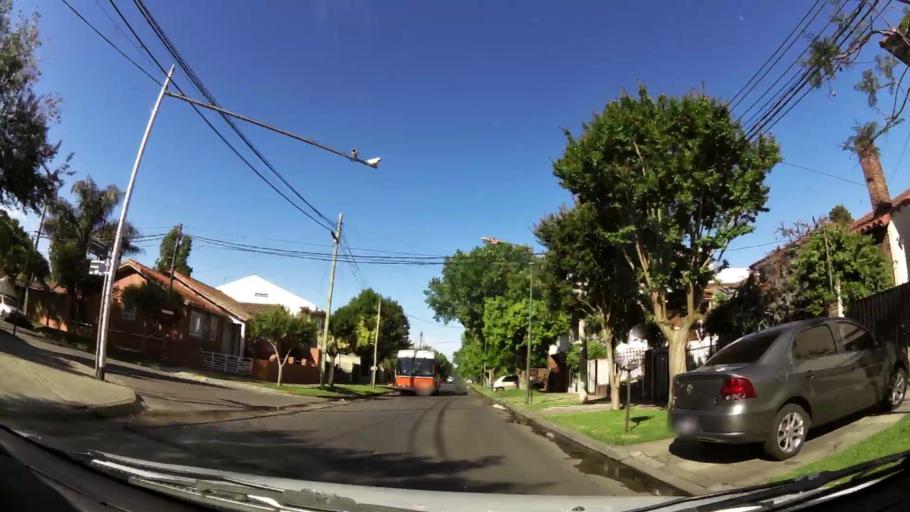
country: AR
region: Buenos Aires
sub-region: Partido de San Isidro
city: San Isidro
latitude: -34.4767
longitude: -58.5330
